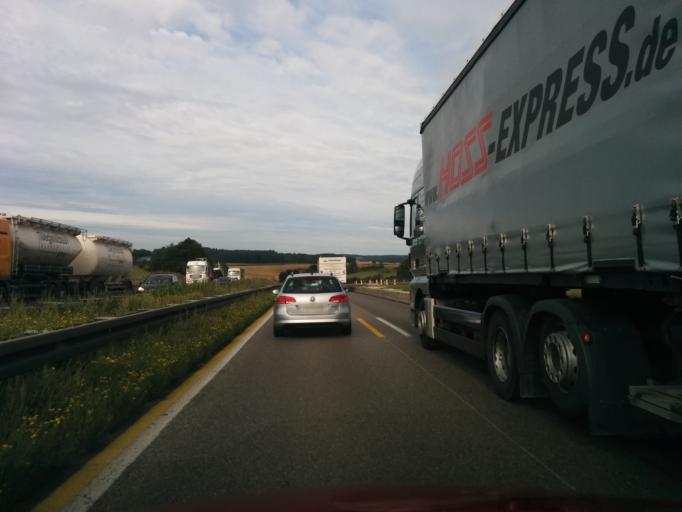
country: DE
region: Baden-Wuerttemberg
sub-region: Tuebingen Region
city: Nellingen
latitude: 48.5202
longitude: 9.8051
